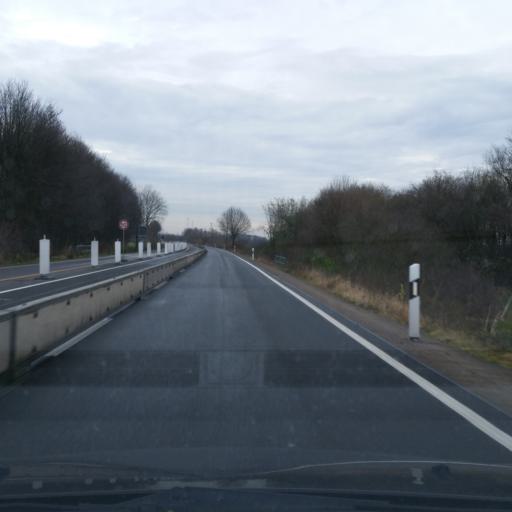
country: DE
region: North Rhine-Westphalia
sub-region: Regierungsbezirk Munster
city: Isselburg
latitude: 51.8105
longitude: 6.5334
